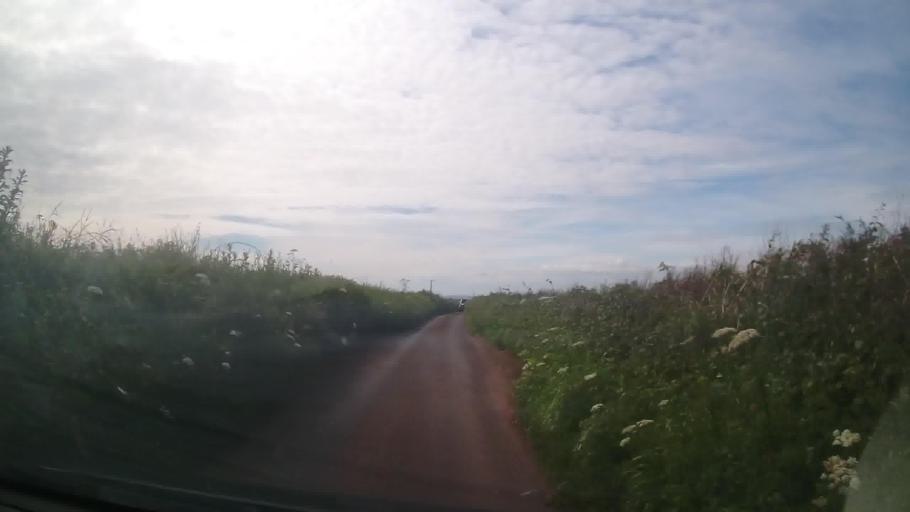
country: GB
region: England
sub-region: Devon
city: Salcombe
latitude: 50.2294
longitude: -3.6660
